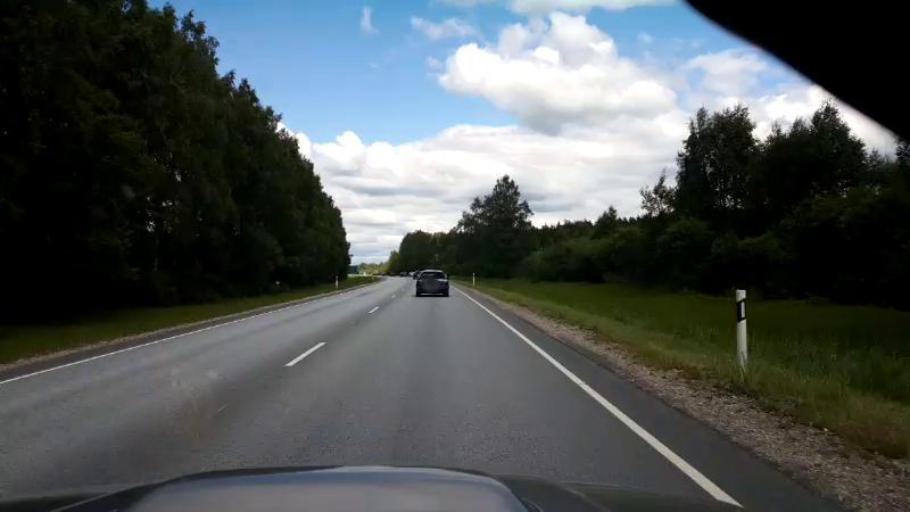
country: EE
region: Paernumaa
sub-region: Sauga vald
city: Sauga
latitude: 58.4569
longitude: 24.5120
